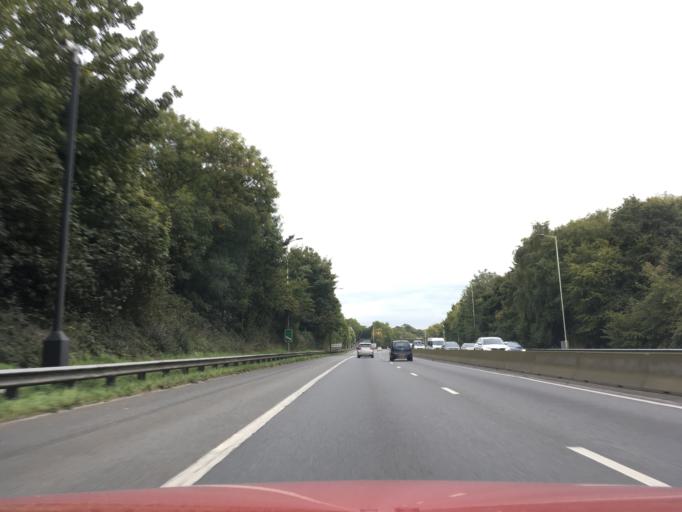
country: GB
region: Wales
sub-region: Cardiff
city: Cardiff
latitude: 51.5173
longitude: -3.1425
